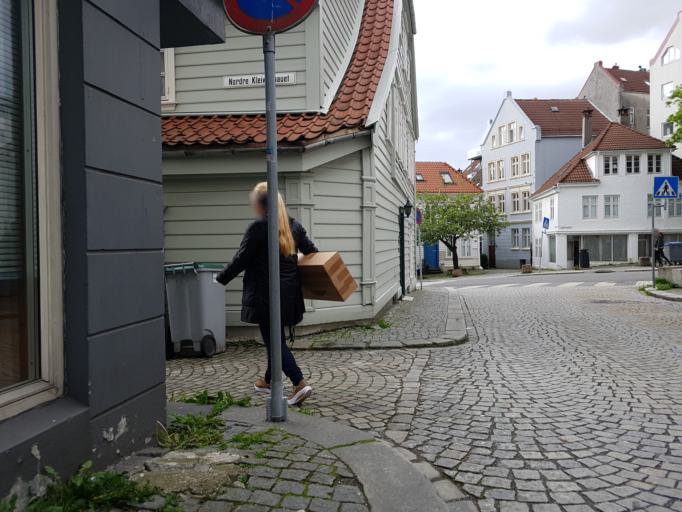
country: NO
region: Hordaland
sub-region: Bergen
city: Bergen
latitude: 60.4000
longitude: 5.3252
